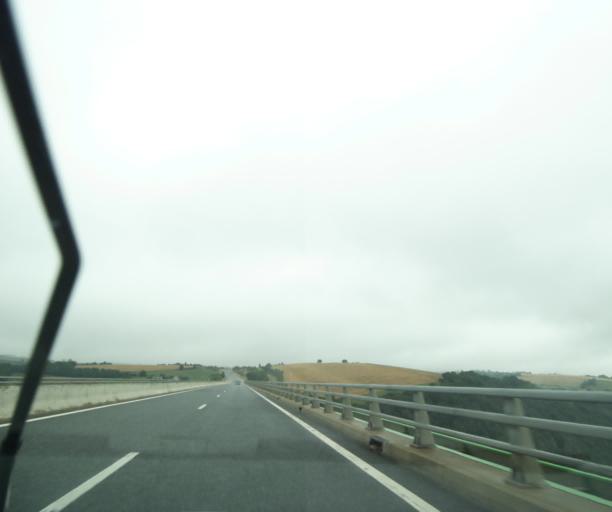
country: FR
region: Midi-Pyrenees
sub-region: Departement de l'Aveyron
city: Naucelle
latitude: 44.1184
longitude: 2.3111
